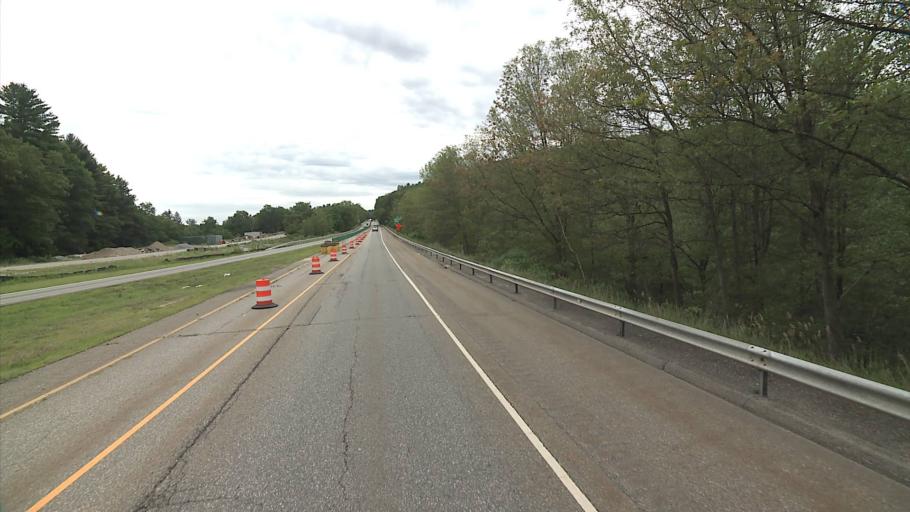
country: US
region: Connecticut
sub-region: Litchfield County
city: Northwest Harwinton
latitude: 41.7418
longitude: -73.1127
